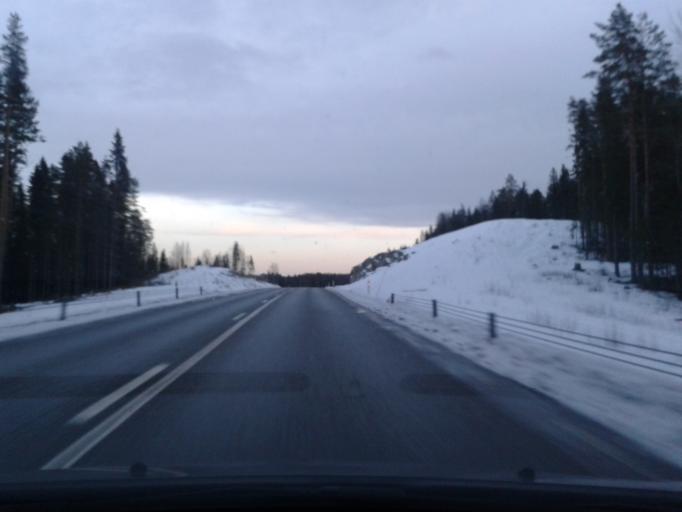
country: SE
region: Vaesternorrland
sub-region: Kramfors Kommun
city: Bollstabruk
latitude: 63.0651
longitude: 17.5887
